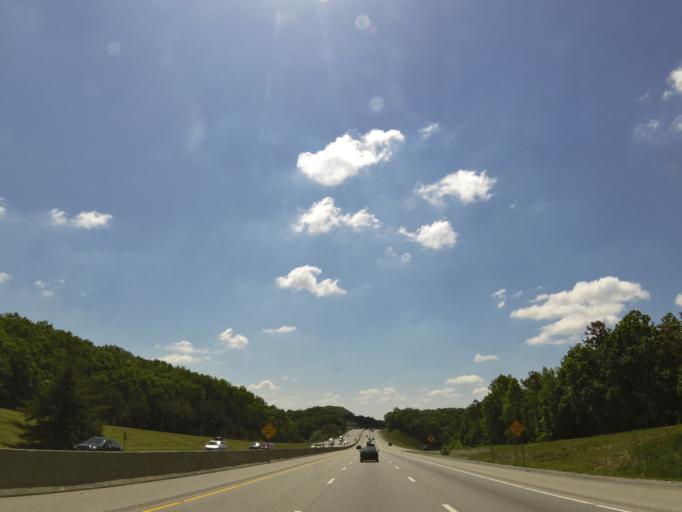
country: US
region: Kentucky
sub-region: Laurel County
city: London
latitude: 37.2255
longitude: -84.2142
